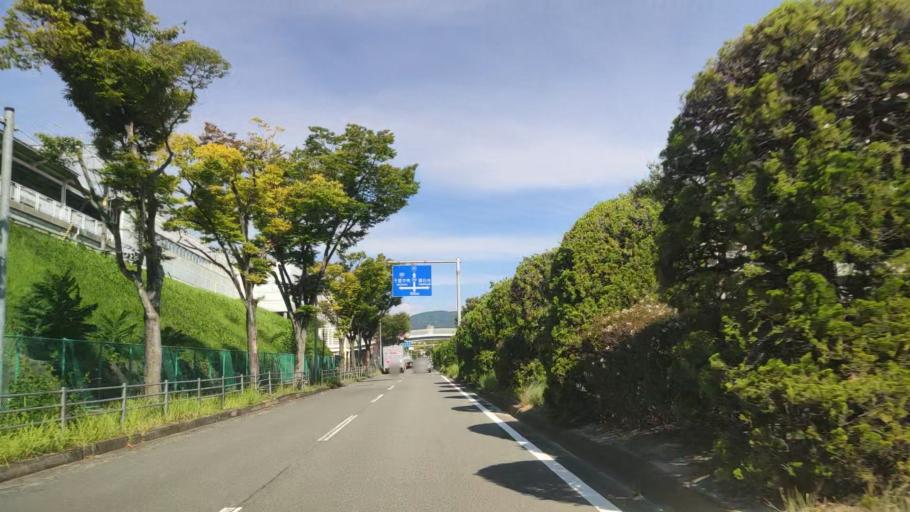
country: JP
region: Osaka
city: Mino
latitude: 34.8193
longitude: 135.5117
